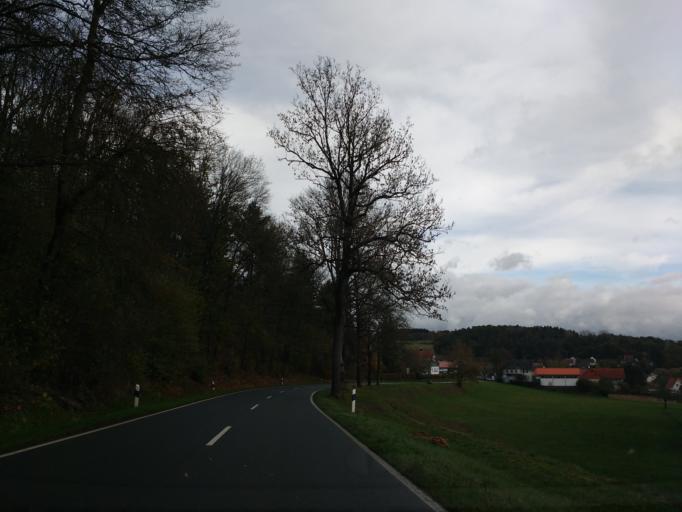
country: DE
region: Hesse
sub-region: Regierungsbezirk Kassel
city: Vohl
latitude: 51.2036
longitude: 8.9363
